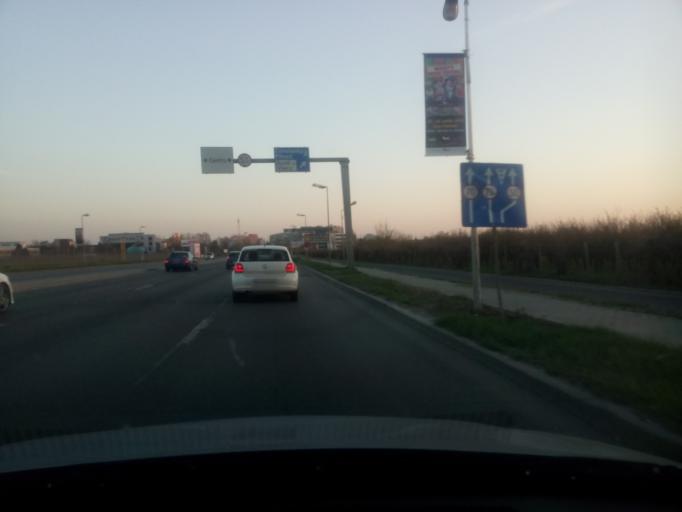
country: RO
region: Ilfov
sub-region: Comuna Otopeni
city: Otopeni
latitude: 44.4996
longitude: 26.0800
